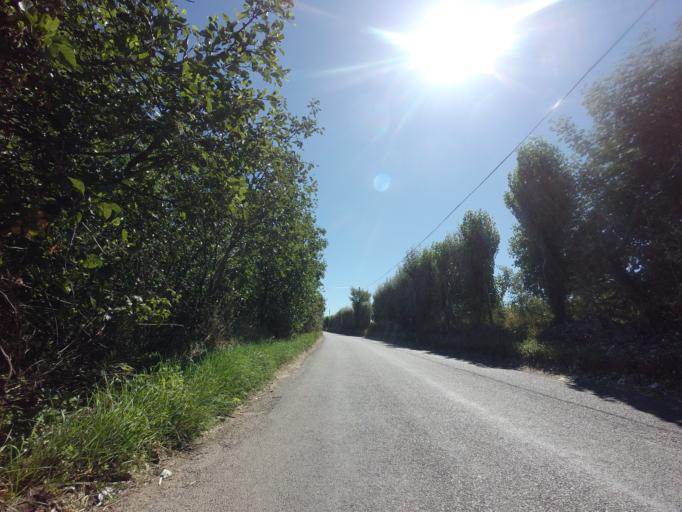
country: GB
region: England
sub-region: Kent
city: Ash
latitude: 51.2833
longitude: 1.2476
